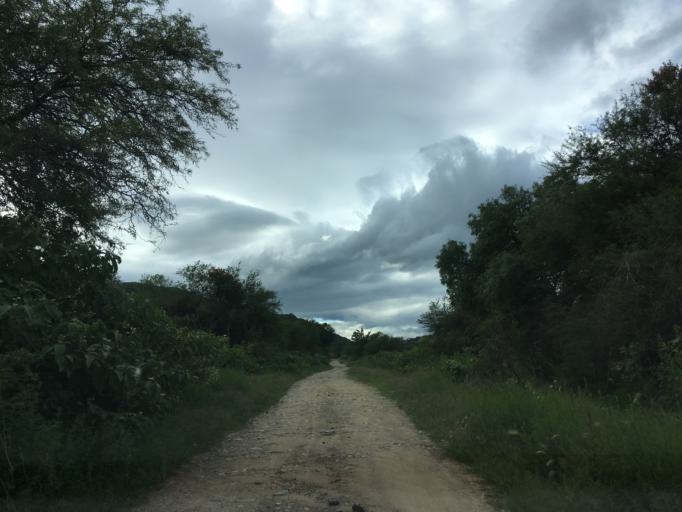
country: MX
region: Guanajuato
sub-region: Acambaro
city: La Ortiga
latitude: 19.9790
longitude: -100.9647
